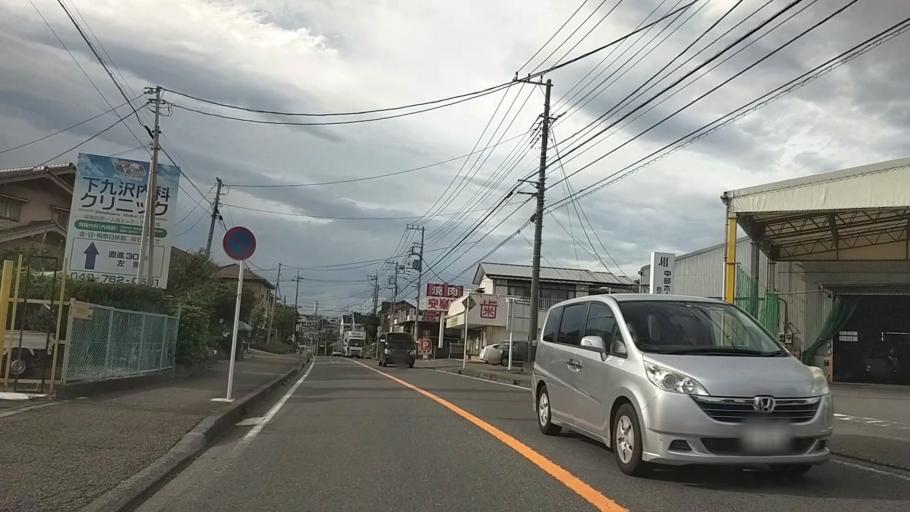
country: JP
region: Tokyo
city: Hachioji
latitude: 35.5689
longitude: 139.3420
